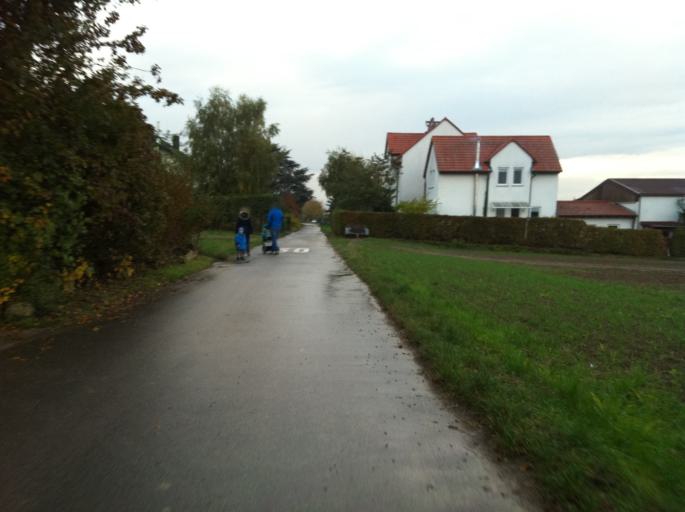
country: DE
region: Rheinland-Pfalz
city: Wackernheim
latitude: 49.9784
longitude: 8.1288
